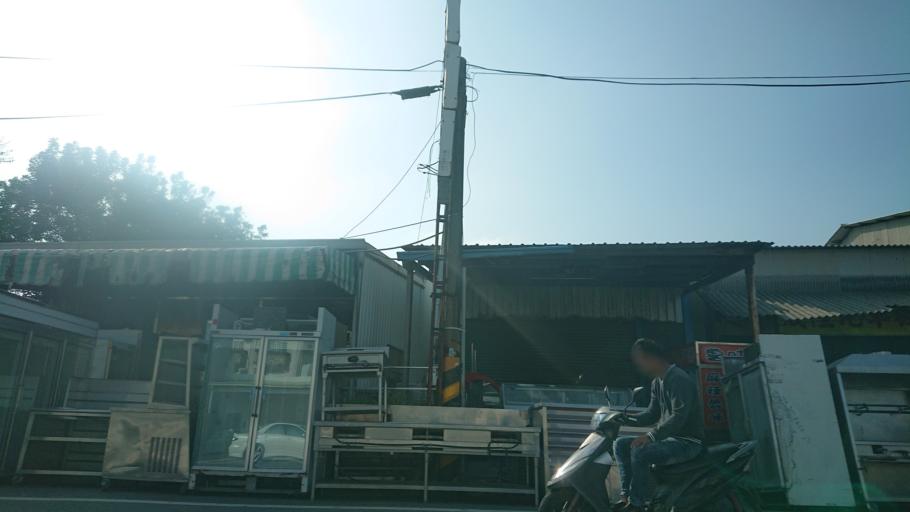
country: TW
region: Taiwan
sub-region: Chiayi
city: Taibao
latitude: 23.4584
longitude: 120.2409
